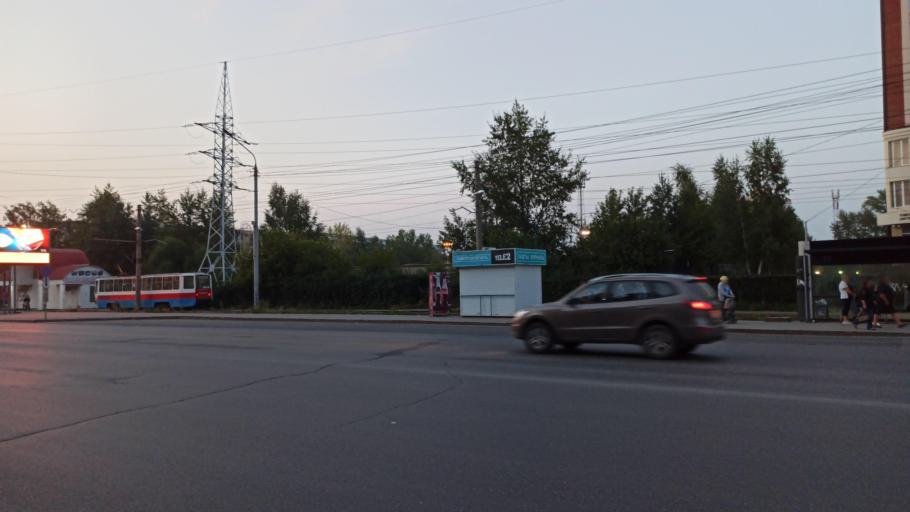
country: RU
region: Tomsk
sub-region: Tomskiy Rayon
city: Tomsk
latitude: 56.4539
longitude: 84.9768
